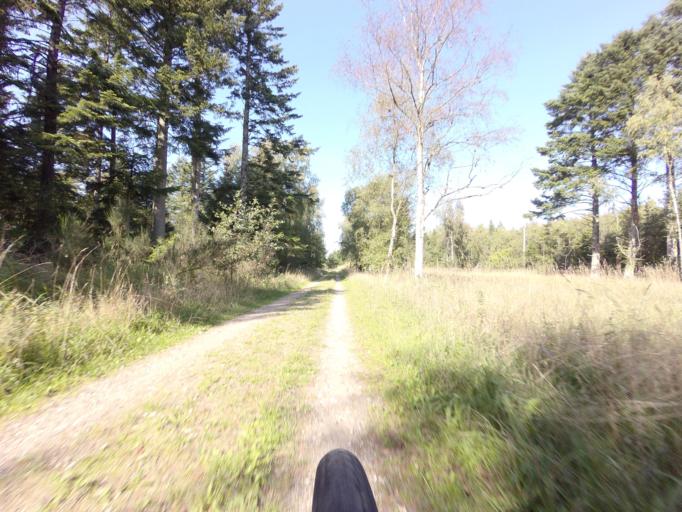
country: DK
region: North Denmark
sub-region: Hjorring Kommune
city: Hirtshals
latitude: 57.5850
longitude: 10.0782
